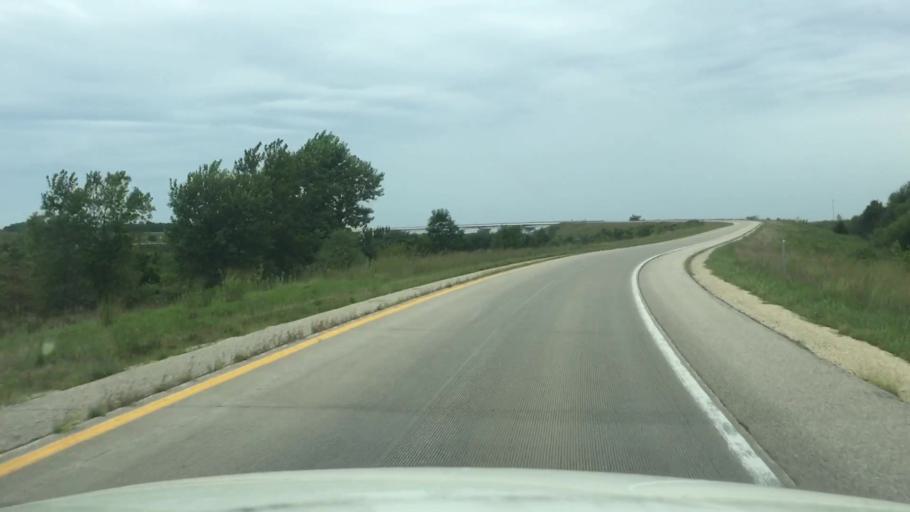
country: US
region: Iowa
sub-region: Polk County
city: West Des Moines
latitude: 41.5233
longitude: -93.7657
